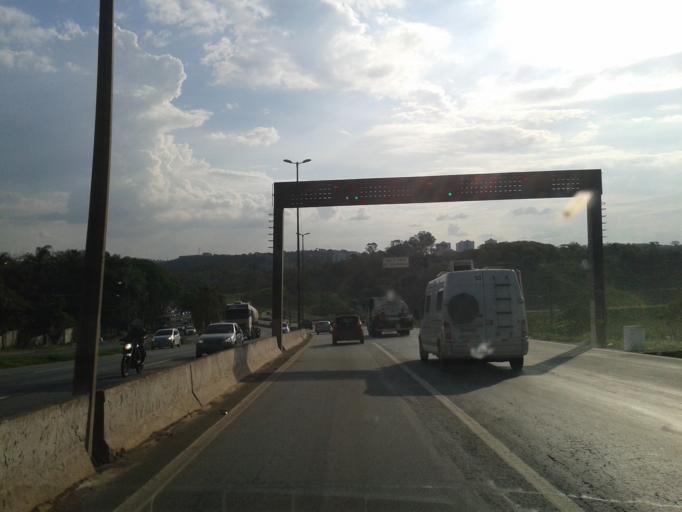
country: BR
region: Minas Gerais
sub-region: Belo Horizonte
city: Belo Horizonte
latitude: -19.8838
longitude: -43.9641
